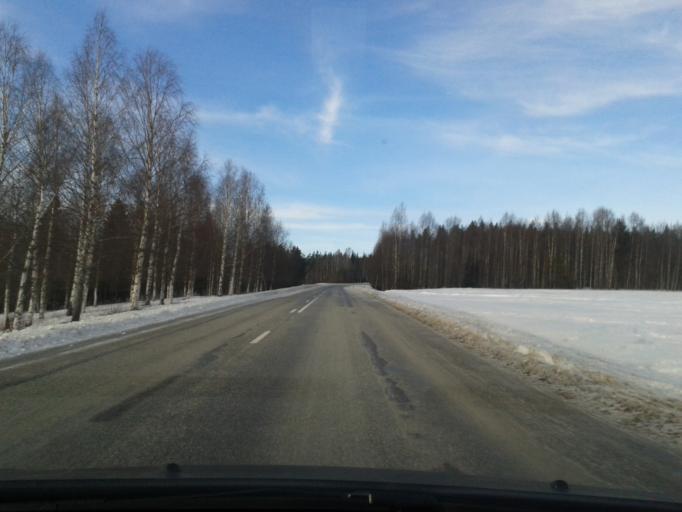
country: SE
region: Vaesternorrland
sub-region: OErnskoeldsviks Kommun
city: Bredbyn
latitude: 63.5739
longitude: 17.9245
